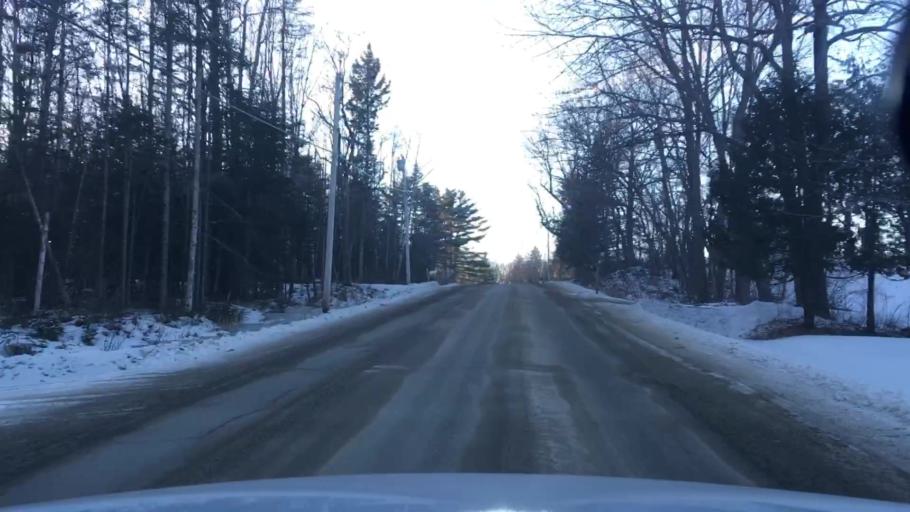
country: US
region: Maine
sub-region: Penobscot County
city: Eddington
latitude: 44.8285
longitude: -68.6507
